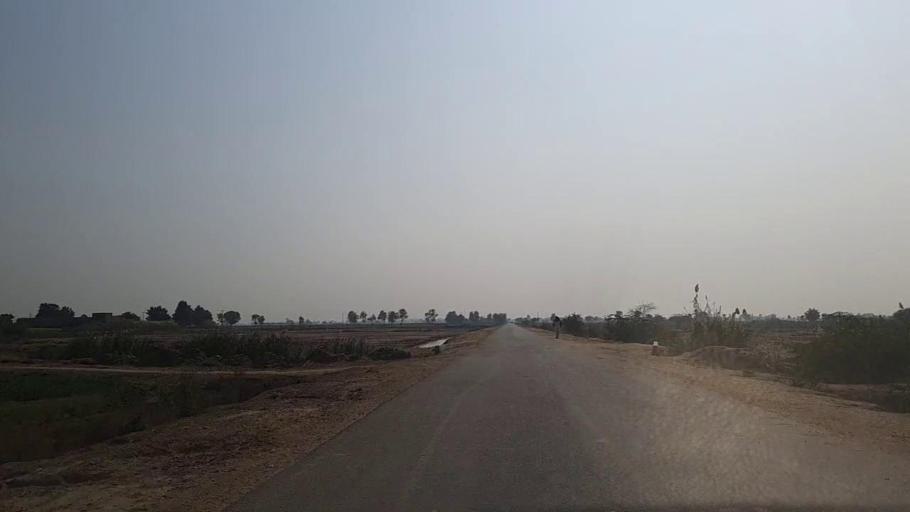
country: PK
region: Sindh
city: Jam Sahib
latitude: 26.3566
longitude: 68.5346
